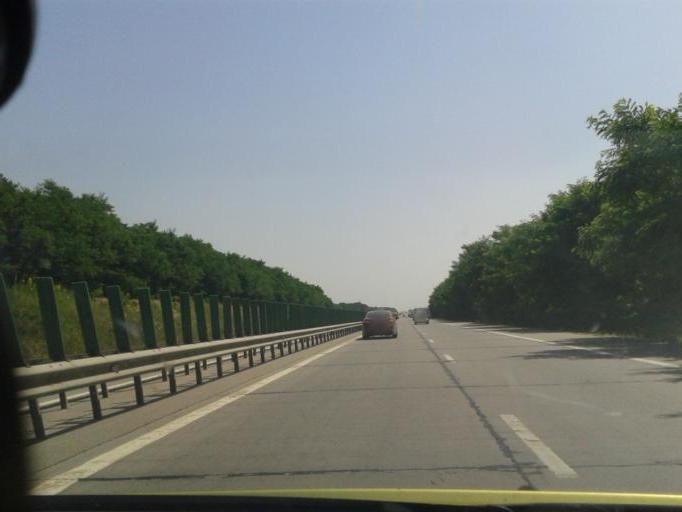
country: RO
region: Ilfov
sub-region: Comuna Cernica
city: Tanganu
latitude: 44.4159
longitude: 26.3069
